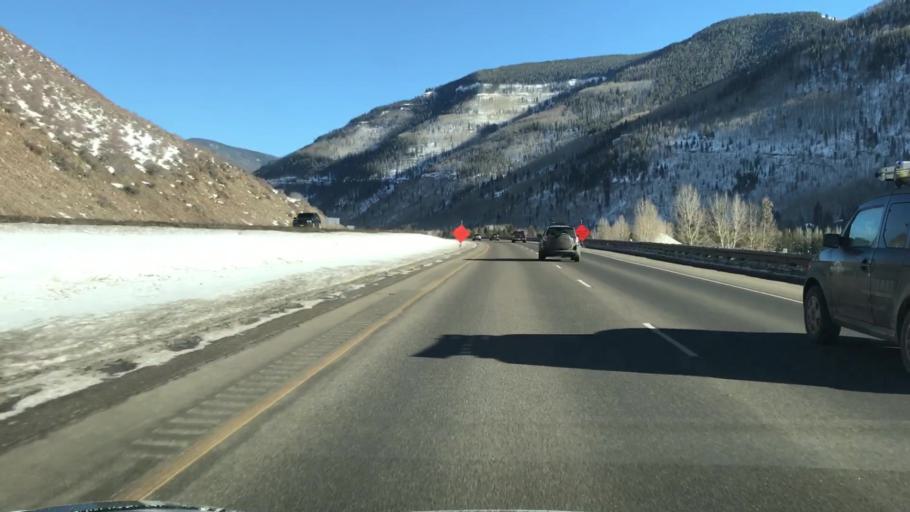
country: US
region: Colorado
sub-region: Eagle County
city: Vail
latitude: 39.6419
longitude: -106.3679
